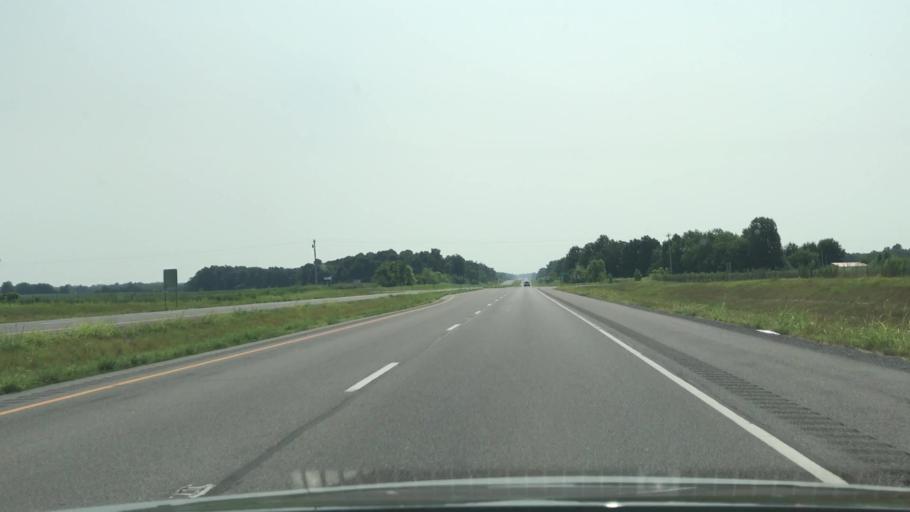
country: US
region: Kentucky
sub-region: Graves County
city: Mayfield
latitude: 36.6754
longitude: -88.5169
